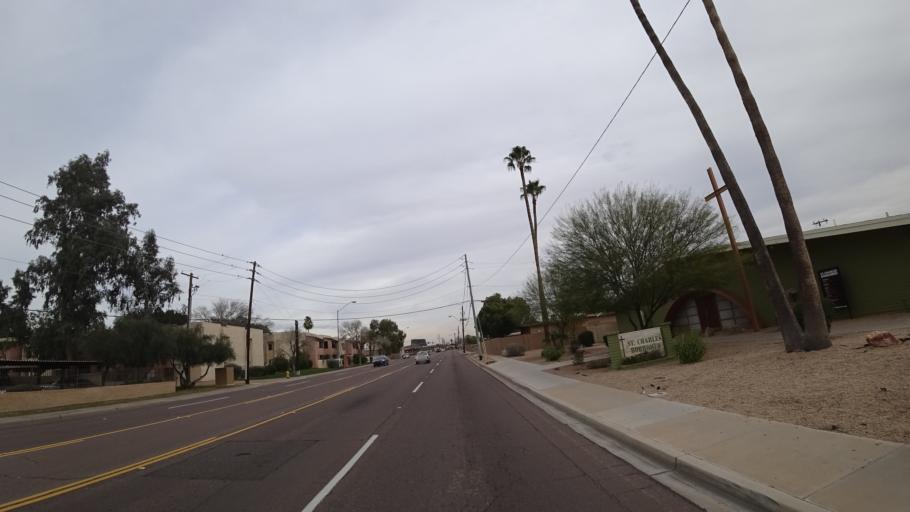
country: US
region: Arizona
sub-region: Maricopa County
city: Peoria
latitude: 33.5809
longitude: -112.2447
